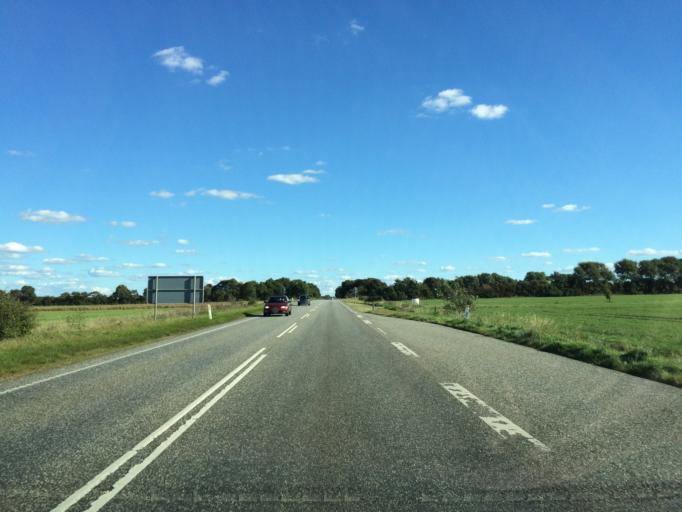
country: DK
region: Central Jutland
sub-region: Holstebro Kommune
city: Holstebro
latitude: 56.3283
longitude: 8.6613
